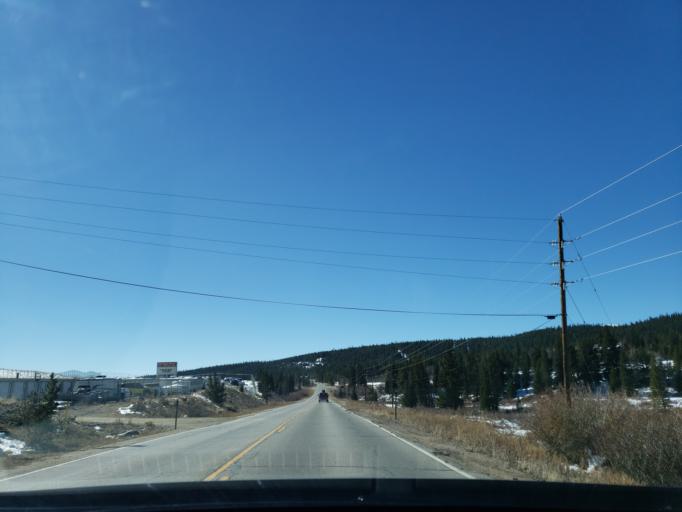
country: US
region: Colorado
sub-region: Park County
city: Fairplay
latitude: 39.2972
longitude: -106.0649
